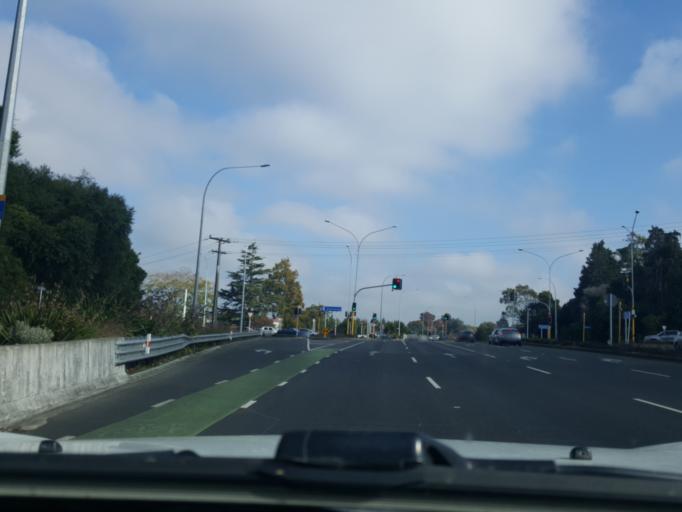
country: NZ
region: Waikato
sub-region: Hamilton City
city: Hamilton
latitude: -37.7412
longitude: 175.2568
